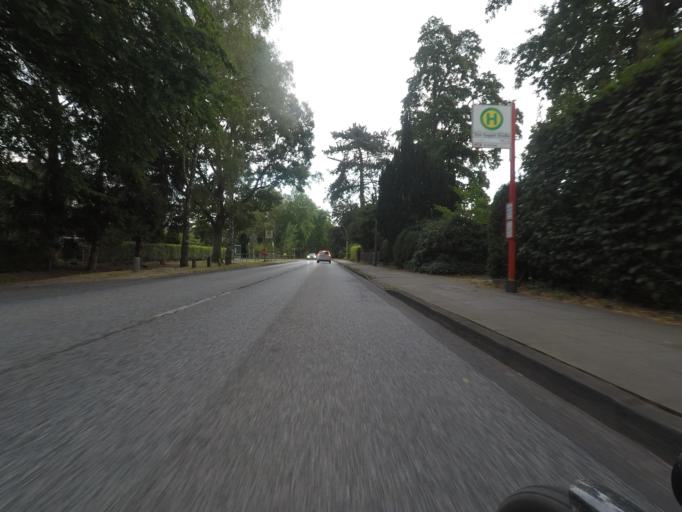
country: DE
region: Hamburg
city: Farmsen-Berne
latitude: 53.6331
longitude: 10.1646
